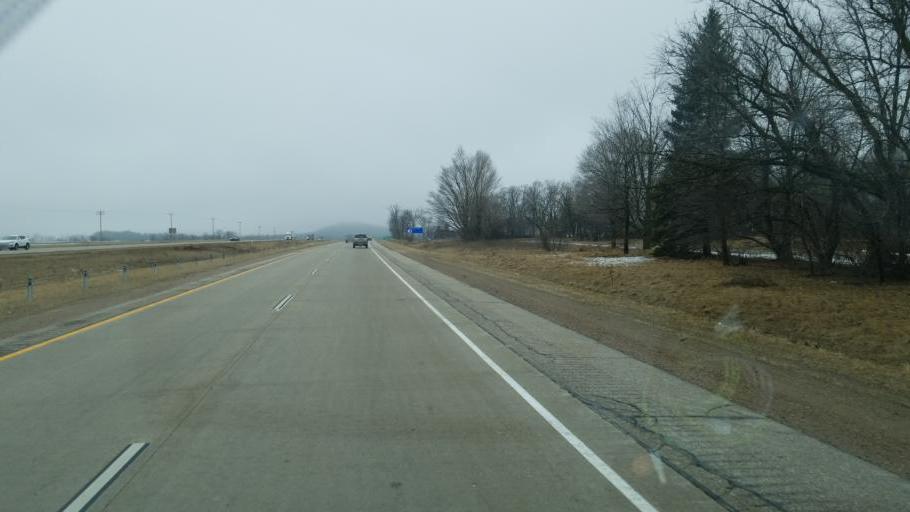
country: US
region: Wisconsin
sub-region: Waupaca County
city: Waupaca
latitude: 44.3295
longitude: -89.0272
